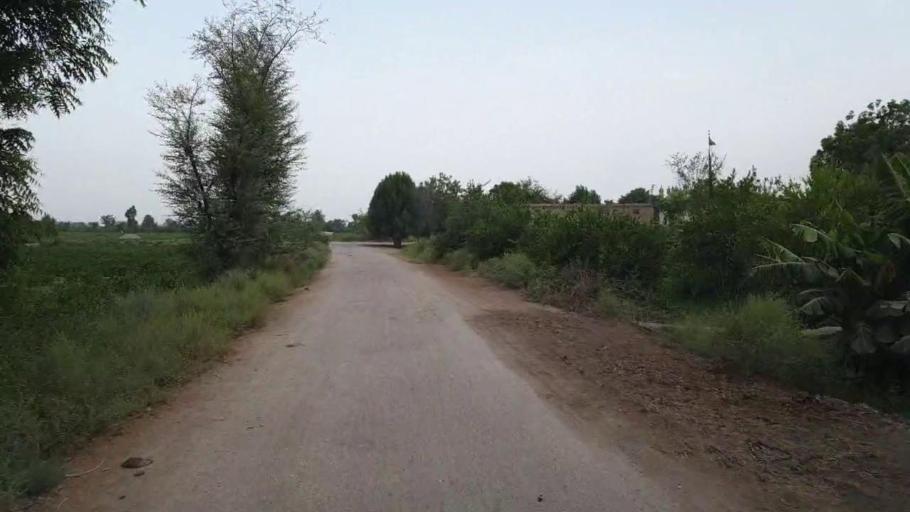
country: PK
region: Sindh
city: Bandhi
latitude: 26.5328
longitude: 68.2042
